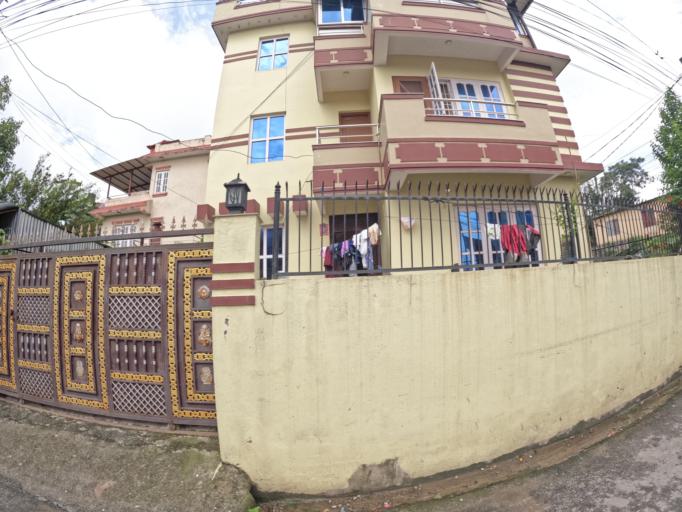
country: NP
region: Central Region
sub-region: Bagmati Zone
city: Kathmandu
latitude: 27.7533
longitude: 85.3208
